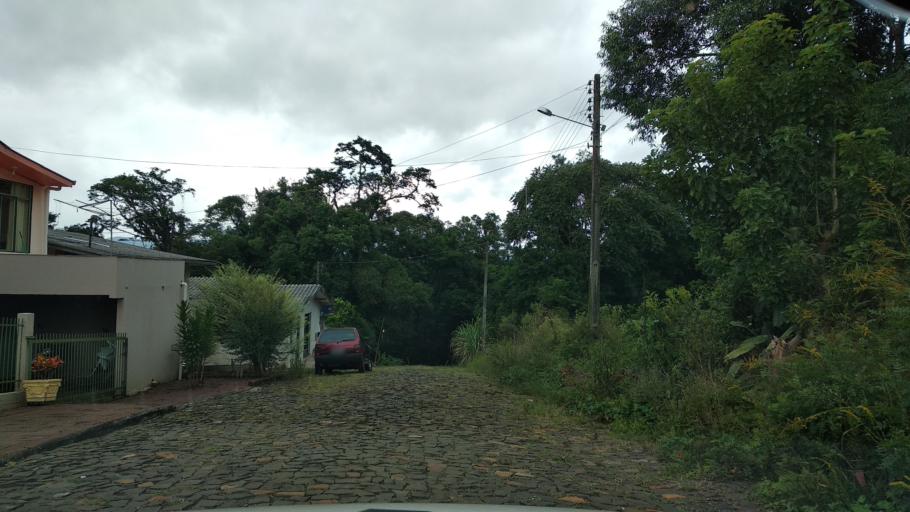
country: BR
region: Santa Catarina
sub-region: Videira
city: Videira
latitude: -26.9855
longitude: -51.1705
